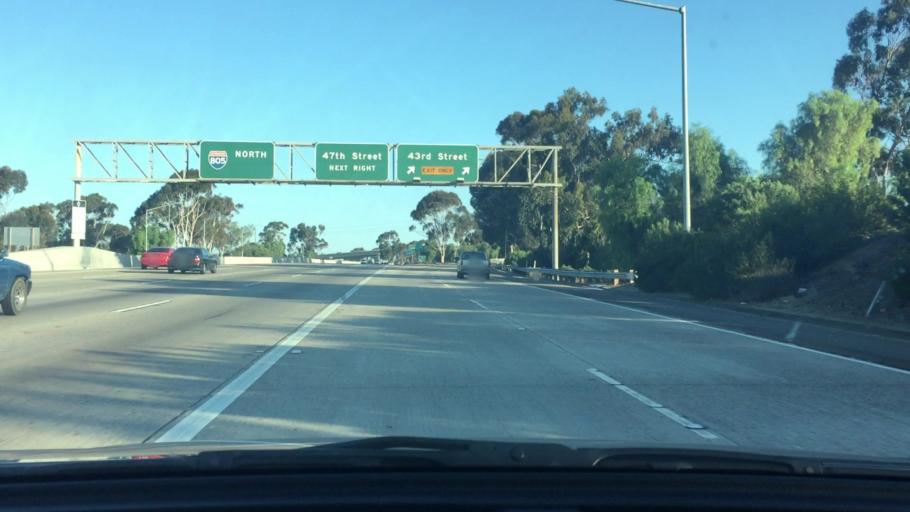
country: US
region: California
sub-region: San Diego County
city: National City
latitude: 32.6853
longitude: -117.0900
